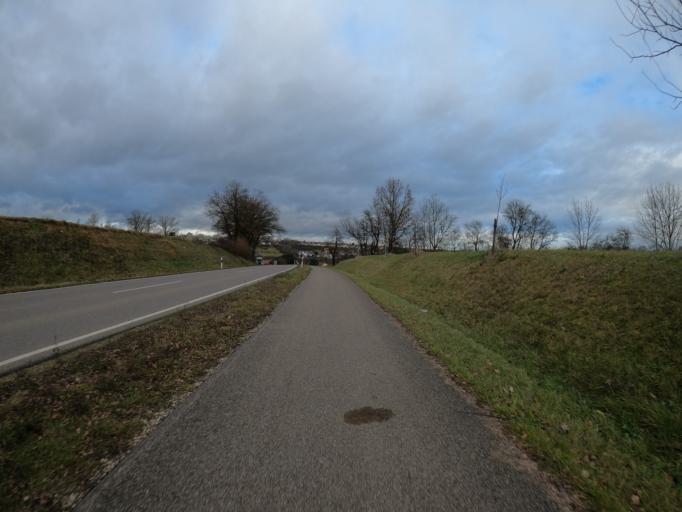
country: DE
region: Baden-Wuerttemberg
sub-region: Regierungsbezirk Stuttgart
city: Waldstetten
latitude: 48.7796
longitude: 9.8387
